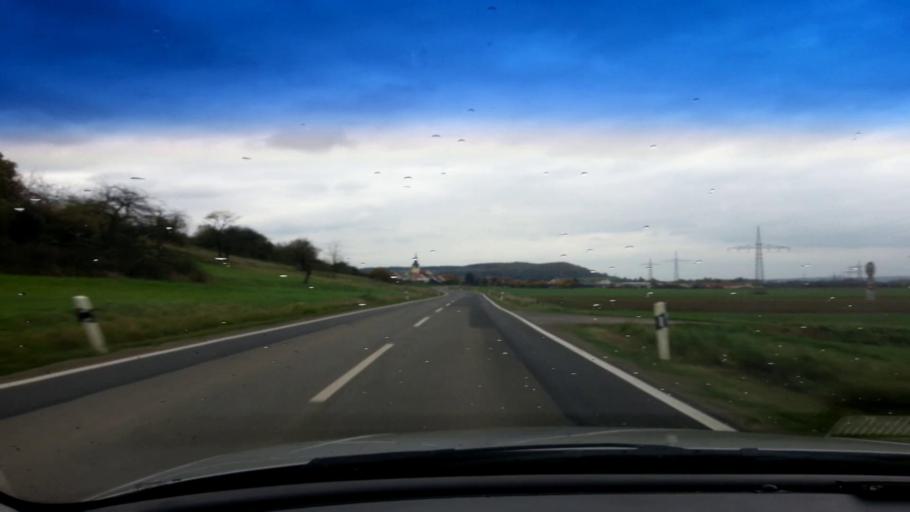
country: DE
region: Bavaria
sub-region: Regierungsbezirk Unterfranken
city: Stettfeld
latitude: 49.9751
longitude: 10.7103
